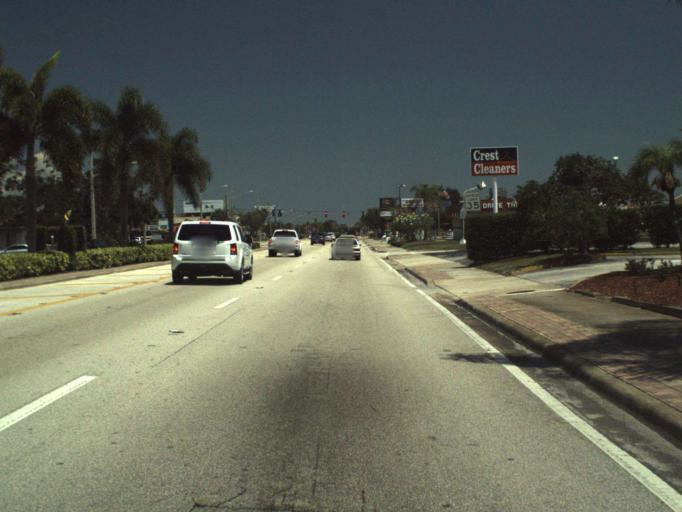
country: US
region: Florida
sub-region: Brevard County
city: Rockledge
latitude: 28.3637
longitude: -80.7001
